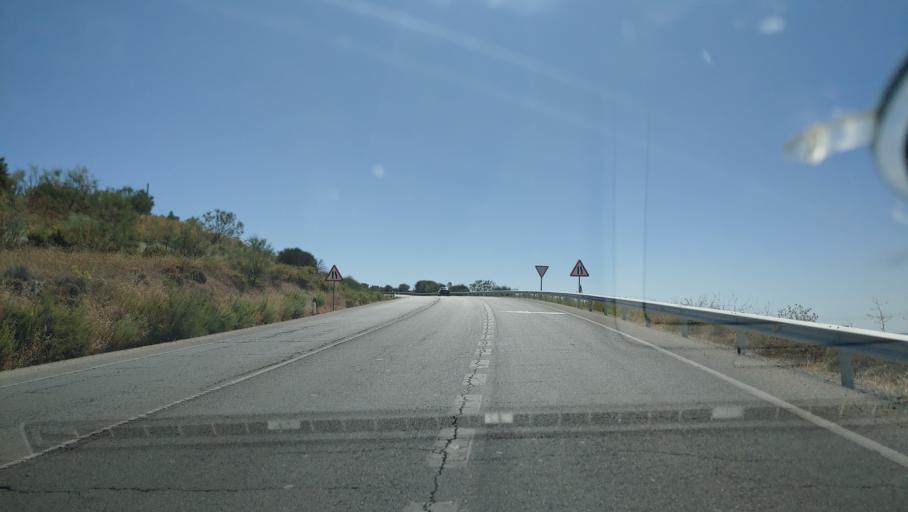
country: ES
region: Andalusia
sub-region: Provincia de Jaen
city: Iznatoraf
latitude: 38.1339
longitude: -3.0538
